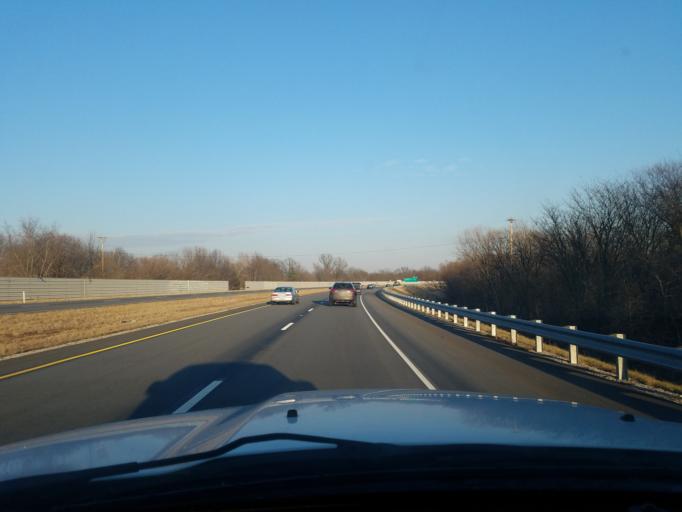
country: US
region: Indiana
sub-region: Vanderburgh County
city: Evansville
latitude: 37.9390
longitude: -87.5171
